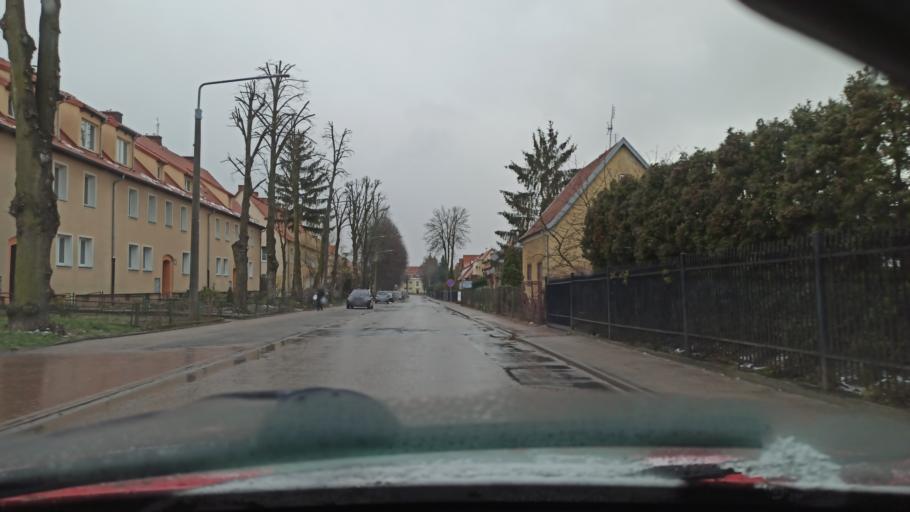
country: PL
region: Warmian-Masurian Voivodeship
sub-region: Powiat elblaski
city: Elblag
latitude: 54.1763
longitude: 19.4129
